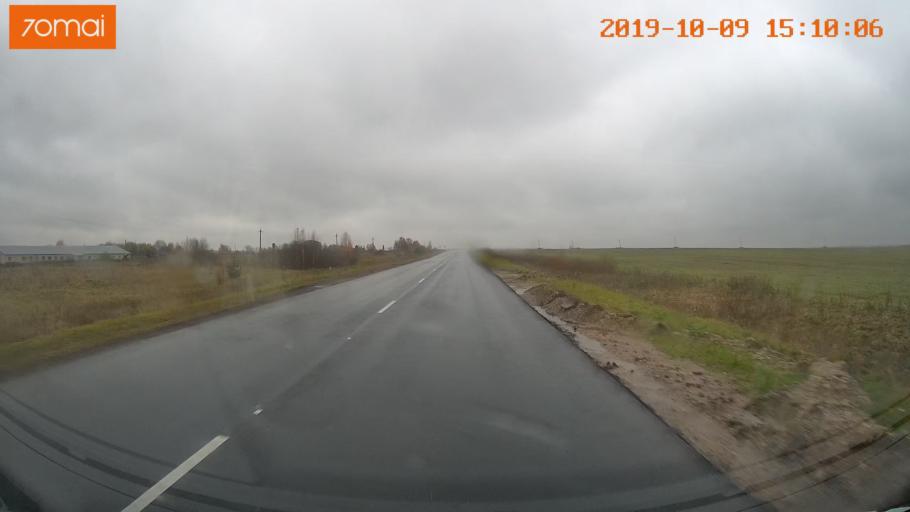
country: RU
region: Kostroma
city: Susanino
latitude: 58.1824
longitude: 41.6449
